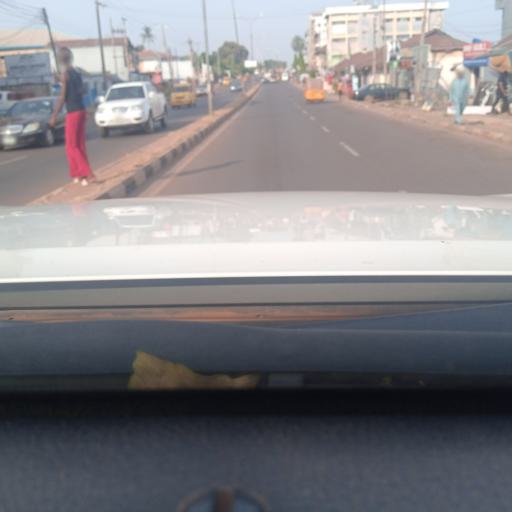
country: NG
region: Enugu
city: Enugu
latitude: 6.4463
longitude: 7.4989
